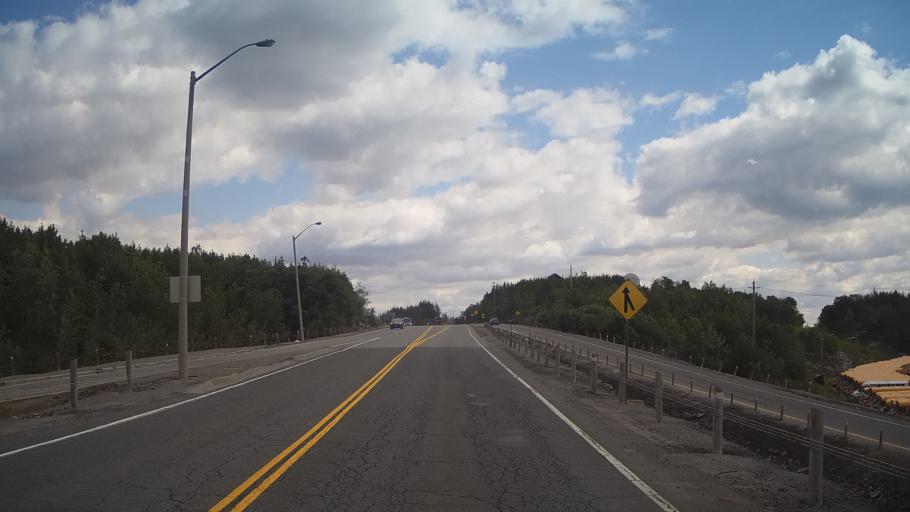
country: CA
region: Ontario
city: Greater Sudbury
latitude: 46.4725
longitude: -81.0387
